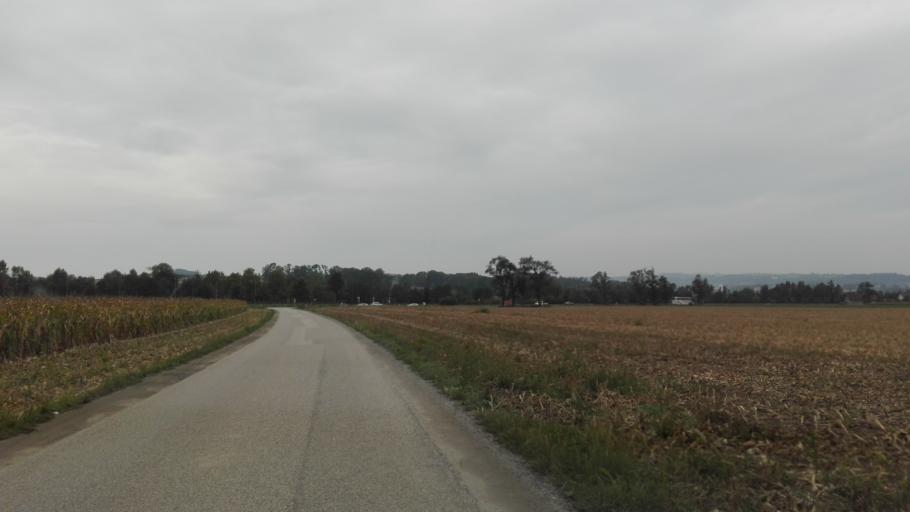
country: AT
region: Upper Austria
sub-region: Wels-Land
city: Buchkirchen
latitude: 48.2881
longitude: 14.0127
